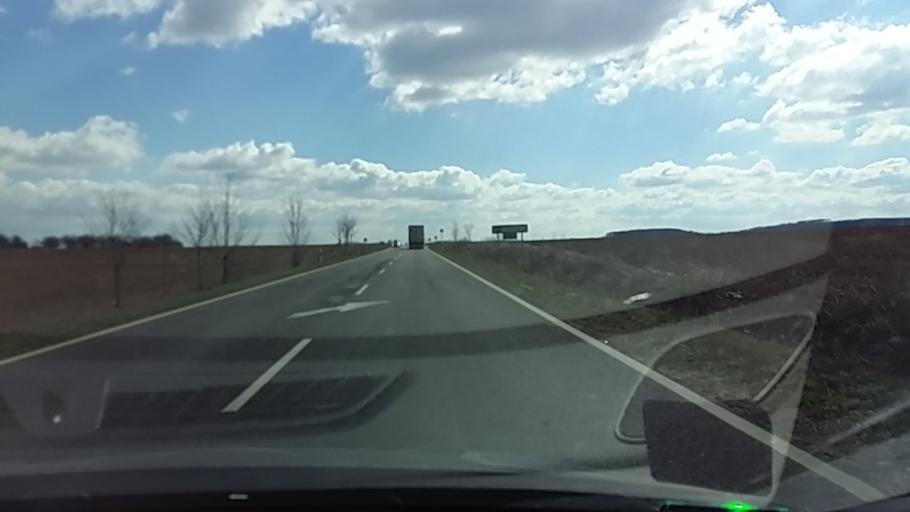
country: HU
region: Baranya
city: Kozarmisleny
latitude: 46.0392
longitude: 18.2723
